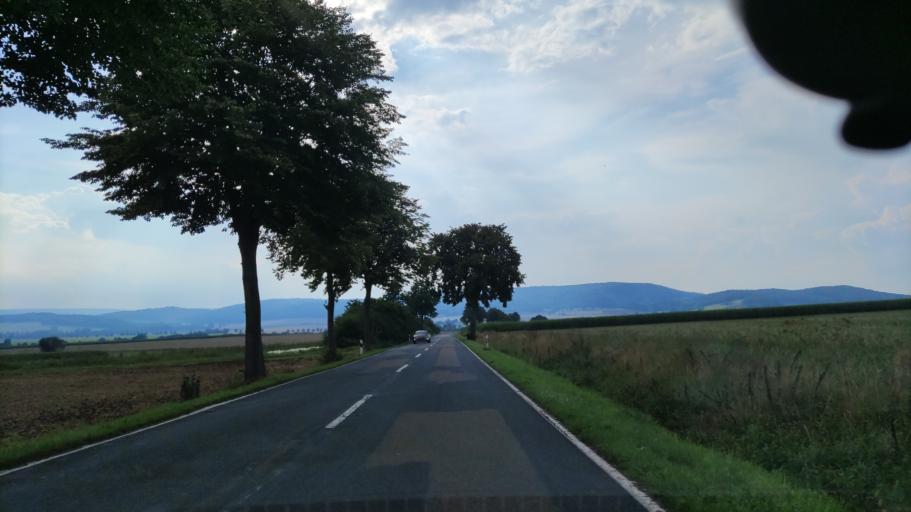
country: DE
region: Lower Saxony
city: Eimen
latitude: 51.8375
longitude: 9.7484
